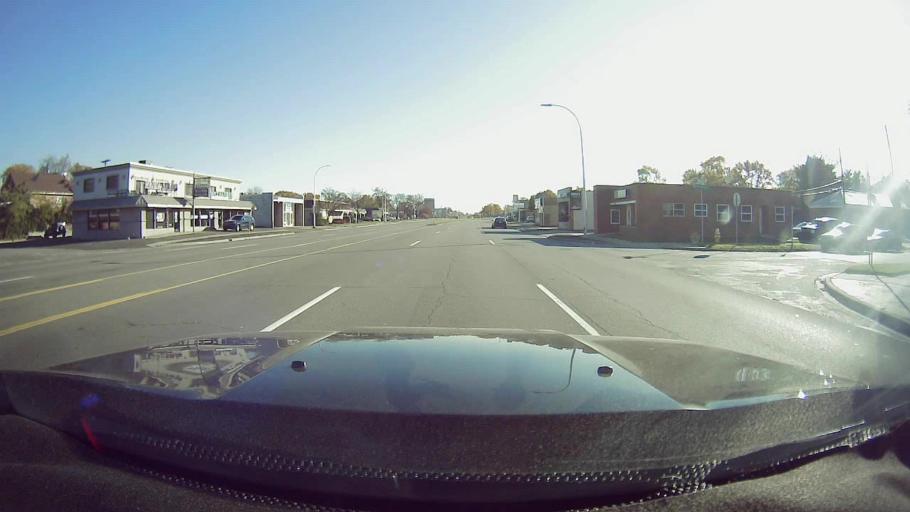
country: US
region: Michigan
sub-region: Wayne County
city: Dearborn Heights
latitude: 42.3270
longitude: -83.2673
